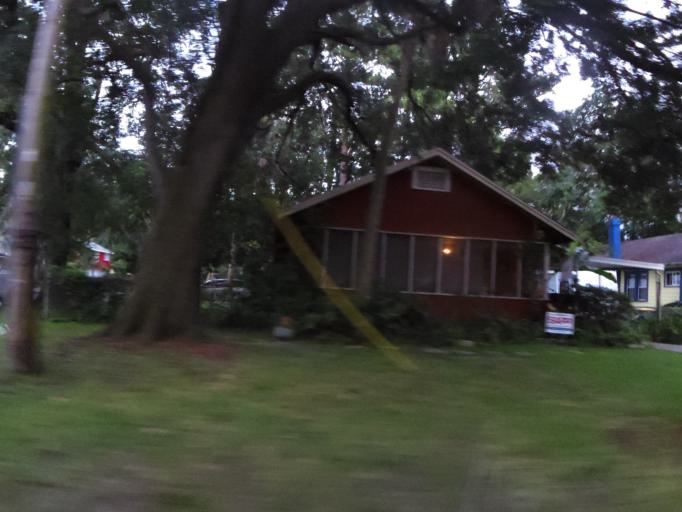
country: US
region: Florida
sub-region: Duval County
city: Jacksonville
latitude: 30.3137
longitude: -81.7177
